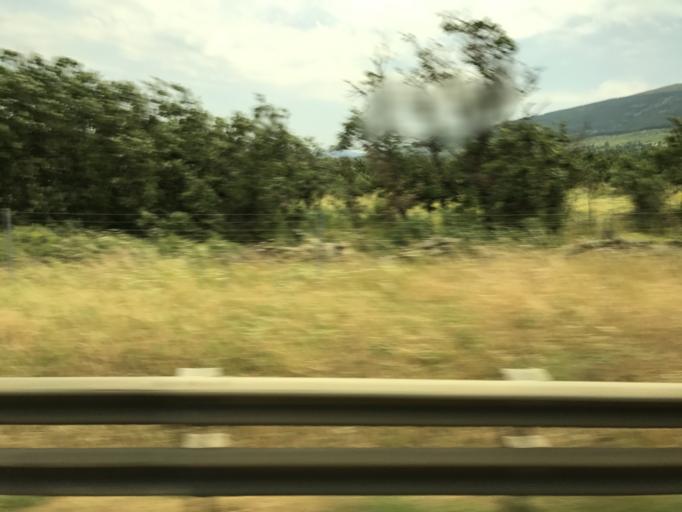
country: ES
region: Castille and Leon
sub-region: Provincia de Segovia
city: Cerezo de Abajo
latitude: 41.1787
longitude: -3.5827
